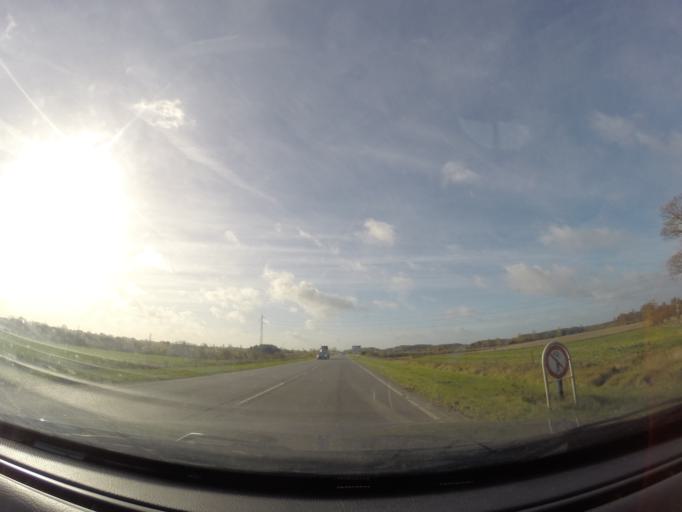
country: DK
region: South Denmark
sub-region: Faaborg-Midtfyn Kommune
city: Ringe
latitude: 55.1926
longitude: 10.5319
